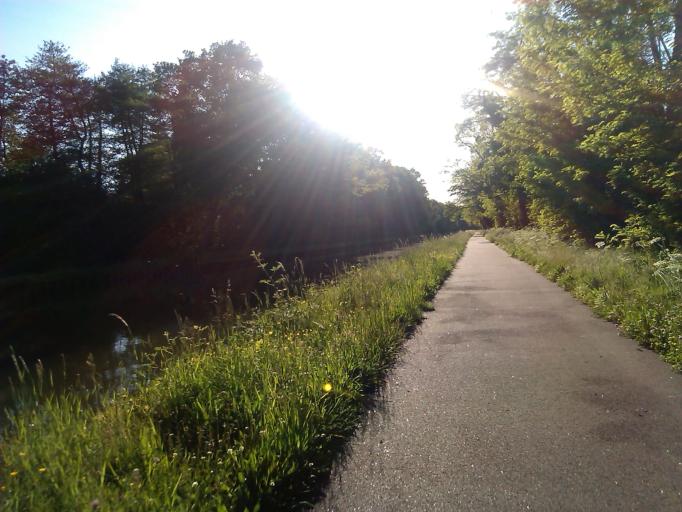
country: FR
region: Auvergne
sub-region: Departement de l'Allier
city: Diou
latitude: 46.5310
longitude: 3.7251
